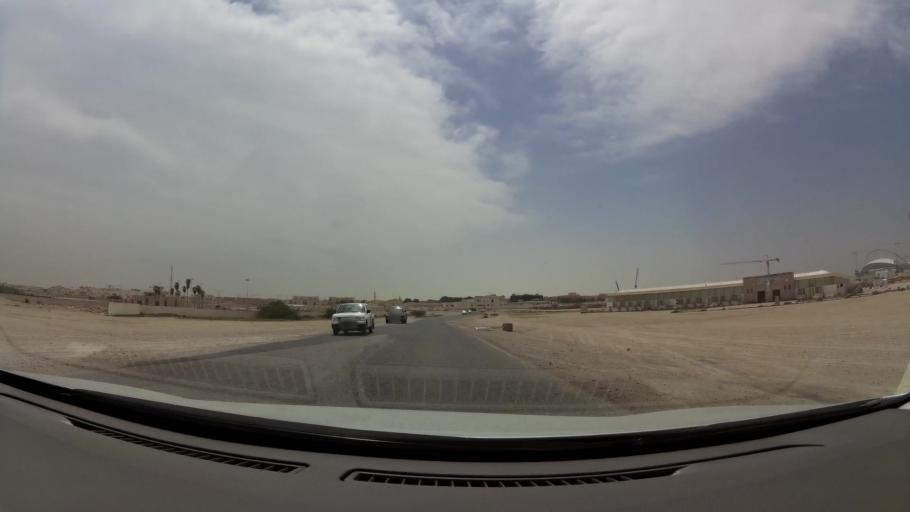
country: QA
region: Baladiyat ar Rayyan
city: Ar Rayyan
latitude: 25.2734
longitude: 51.4607
